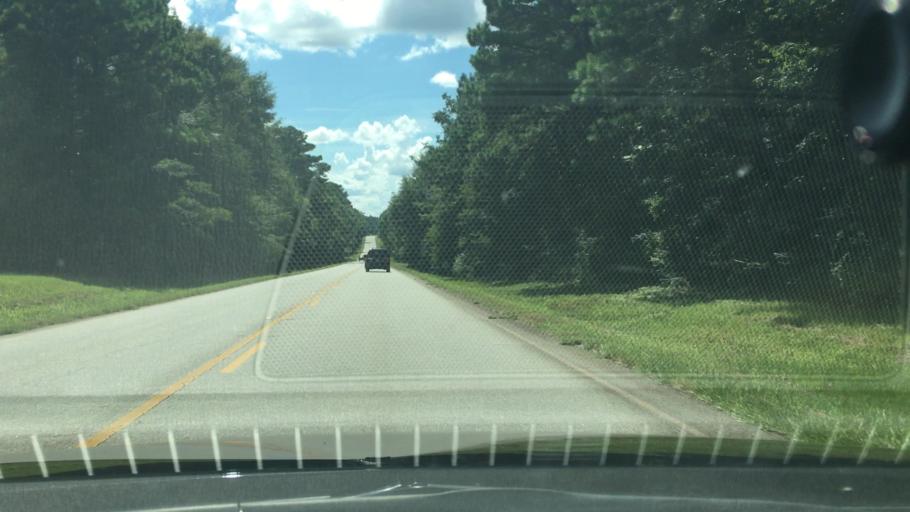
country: US
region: Georgia
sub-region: Jasper County
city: Monticello
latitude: 33.3036
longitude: -83.6254
